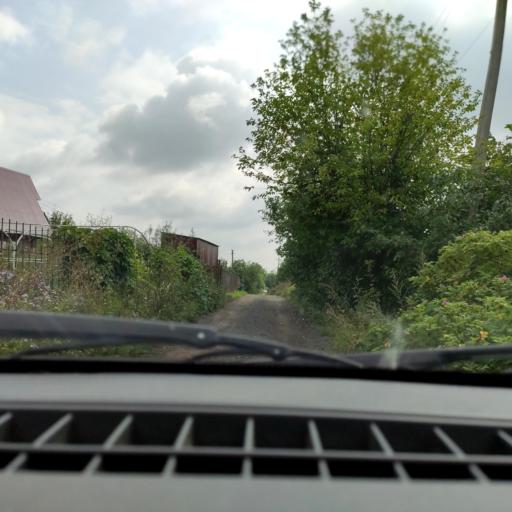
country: RU
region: Bashkortostan
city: Mikhaylovka
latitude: 54.8307
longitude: 55.8316
